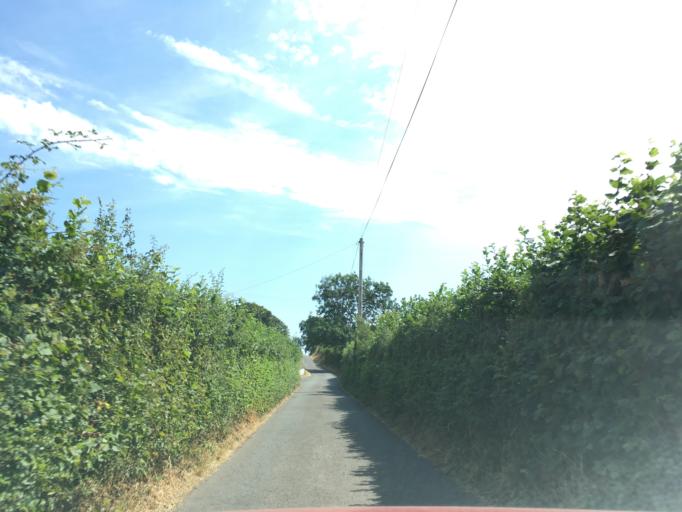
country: GB
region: Wales
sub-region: Newport
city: Llanvaches
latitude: 51.6112
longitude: -2.8505
